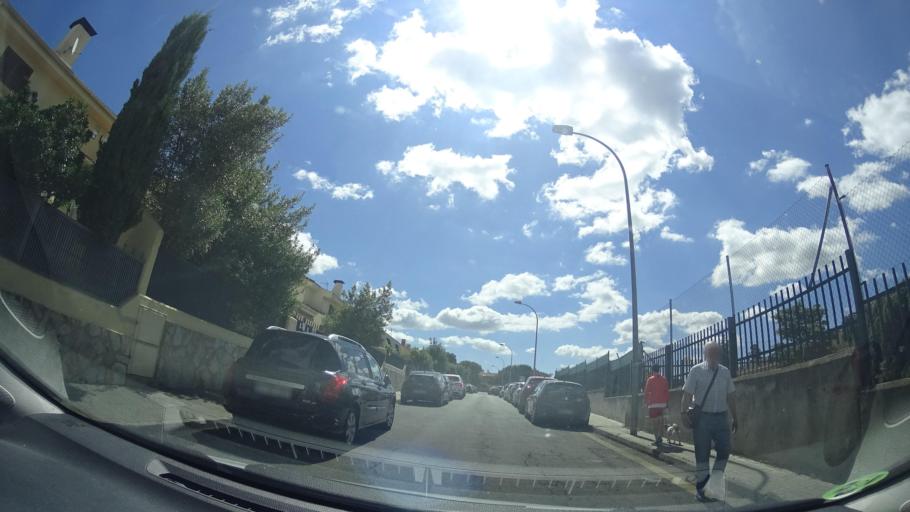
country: ES
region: Madrid
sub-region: Provincia de Madrid
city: Collado-Villalba
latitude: 40.6265
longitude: -3.9996
